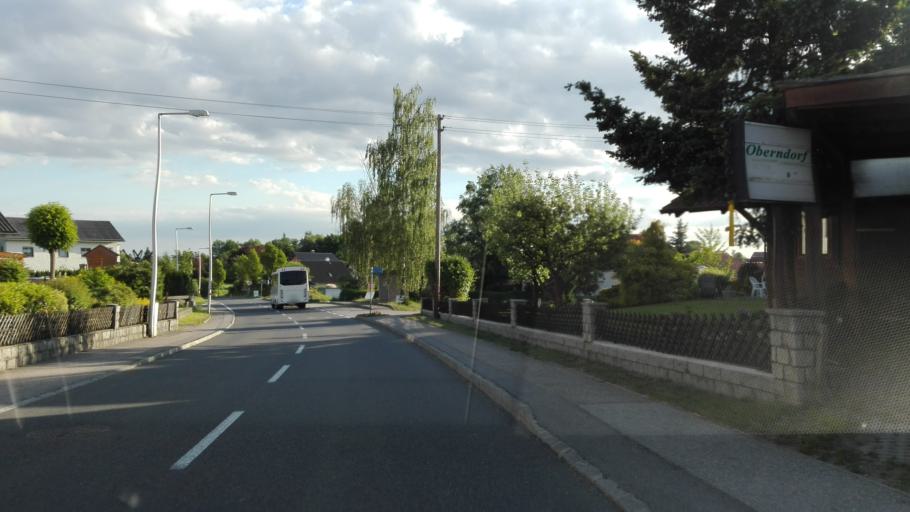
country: AT
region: Upper Austria
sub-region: Politischer Bezirk Urfahr-Umgebung
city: Engerwitzdorf
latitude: 48.3627
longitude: 14.5346
